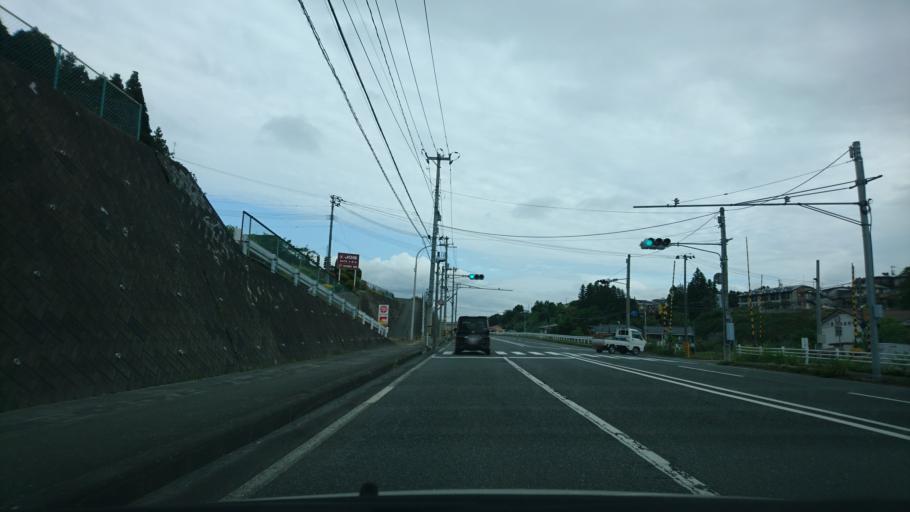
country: JP
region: Iwate
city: Ichinoseki
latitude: 38.9163
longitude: 141.1416
